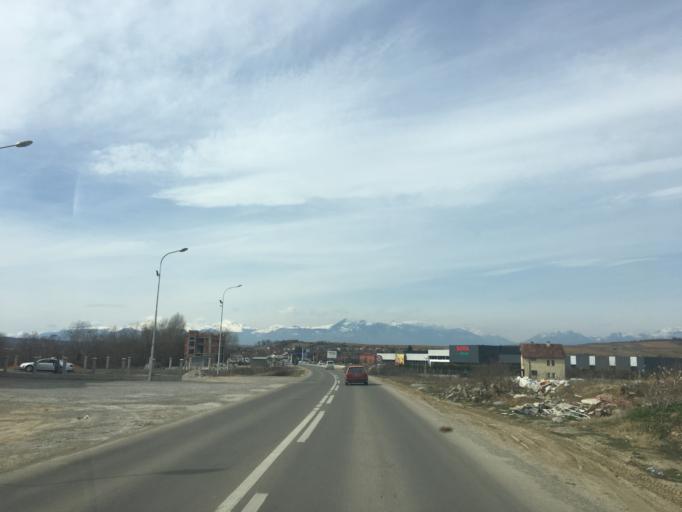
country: XK
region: Pec
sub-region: Komuna e Klines
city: Klina
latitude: 42.5930
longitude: 20.5733
